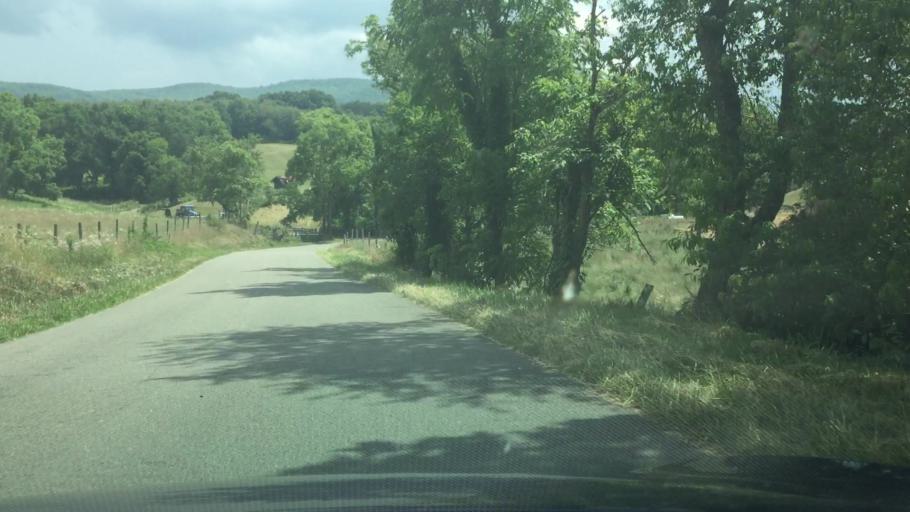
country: US
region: Virginia
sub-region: Wythe County
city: Wytheville
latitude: 36.9367
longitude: -81.0266
